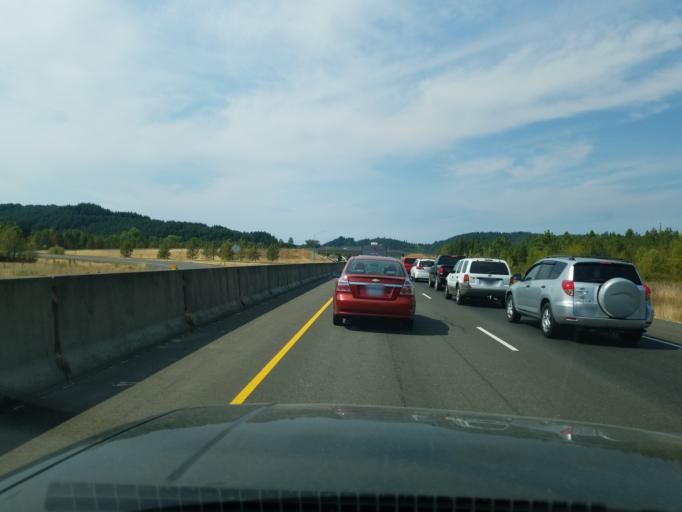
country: US
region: Oregon
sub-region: Yamhill County
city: Willamina
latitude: 45.0530
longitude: -123.5381
